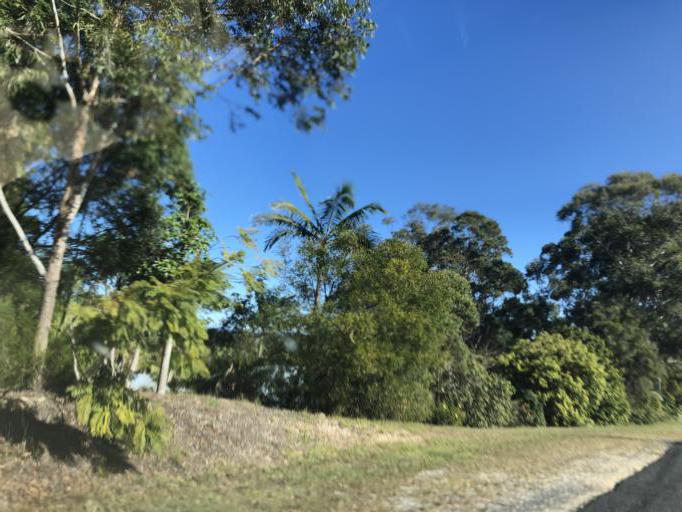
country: AU
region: New South Wales
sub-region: Nambucca Shire
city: Nambucca
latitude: -30.6798
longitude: 152.9690
